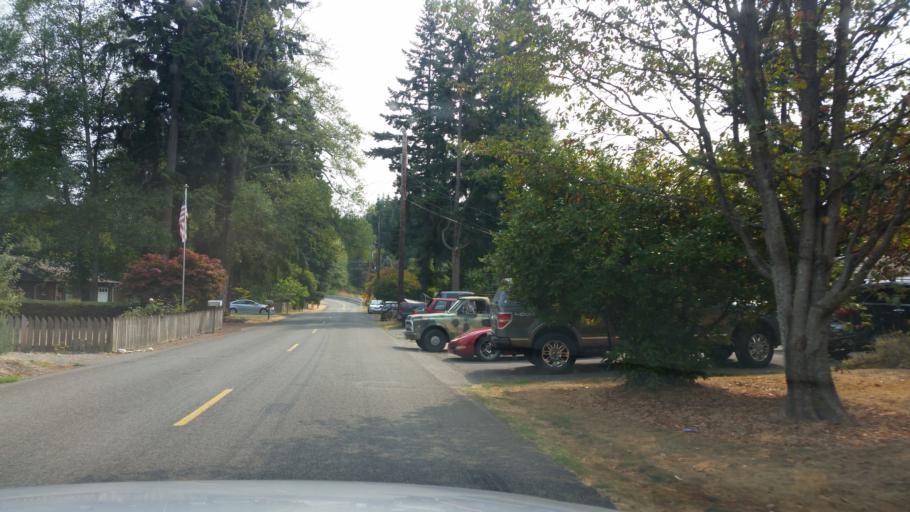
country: US
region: Washington
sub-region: Snohomish County
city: Lynnwood
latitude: 47.8331
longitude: -122.3306
